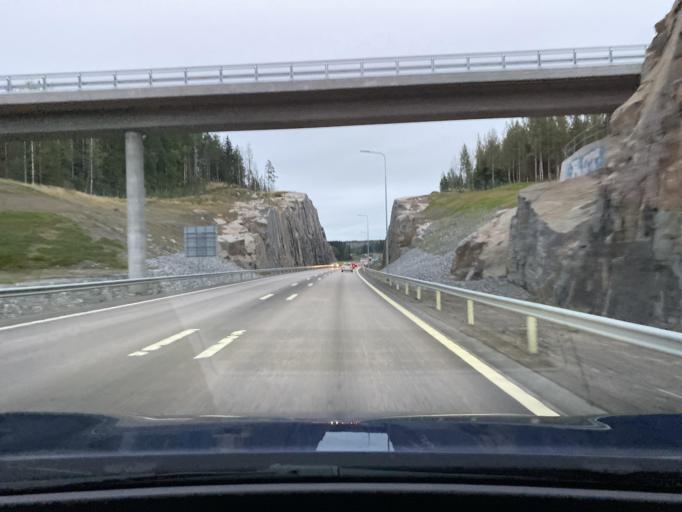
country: FI
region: Paijanne Tavastia
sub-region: Lahti
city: Hollola
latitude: 60.9577
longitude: 25.5560
